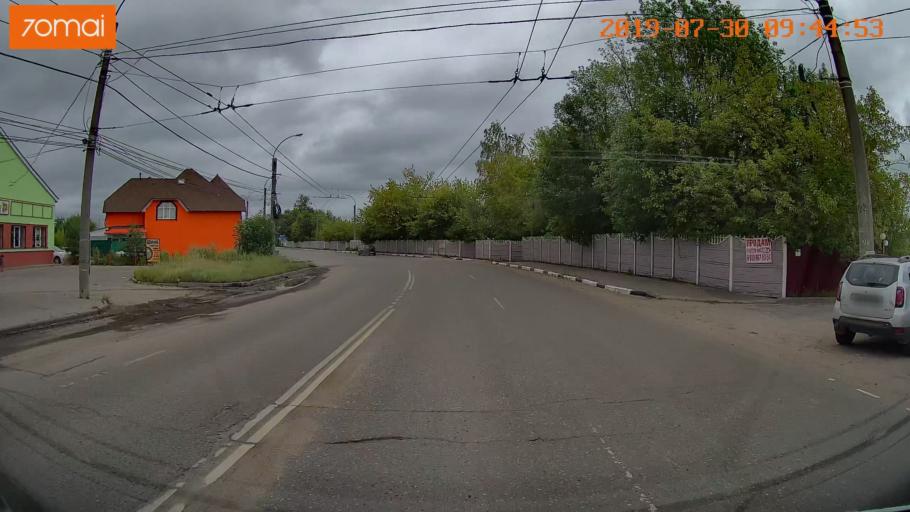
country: RU
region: Ivanovo
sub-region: Gorod Ivanovo
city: Ivanovo
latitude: 56.9465
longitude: 40.9717
